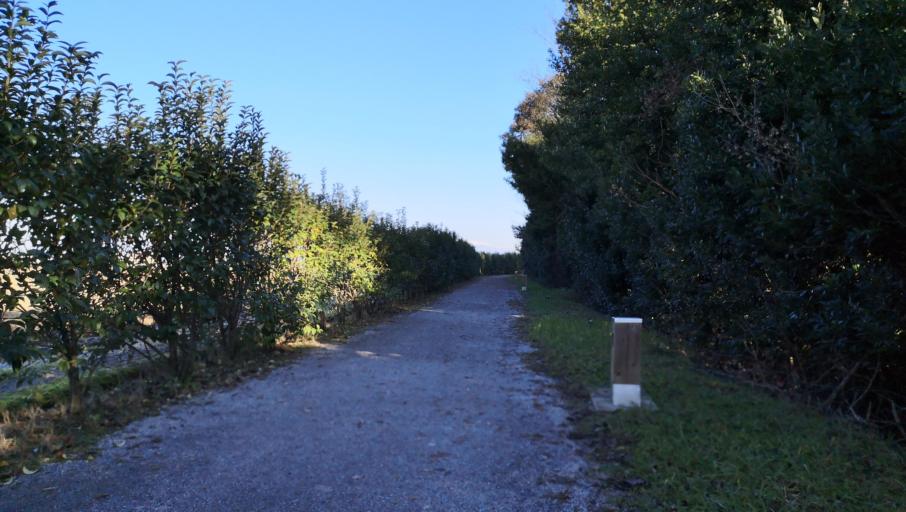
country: IT
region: Friuli Venezia Giulia
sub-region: Provincia di Udine
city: Santa Maria la Longa
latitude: 45.9233
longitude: 13.2935
